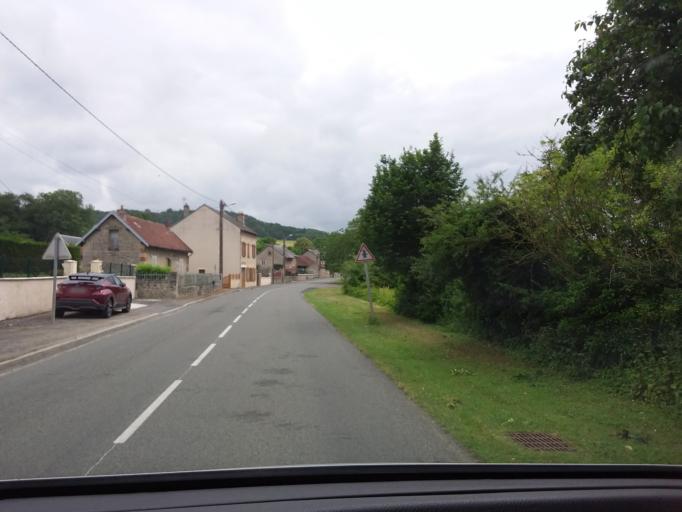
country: FR
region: Picardie
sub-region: Departement de l'Aisne
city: Vailly-sur-Aisne
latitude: 49.4029
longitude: 3.5693
